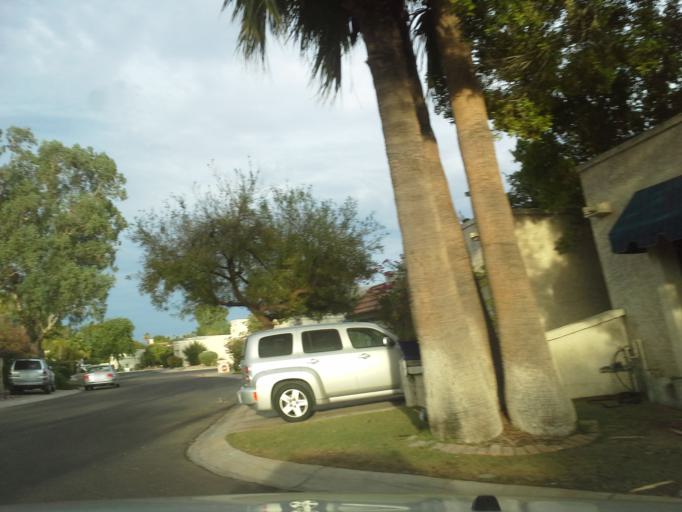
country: US
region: Arizona
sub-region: Maricopa County
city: Guadalupe
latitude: 33.3680
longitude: -111.9757
